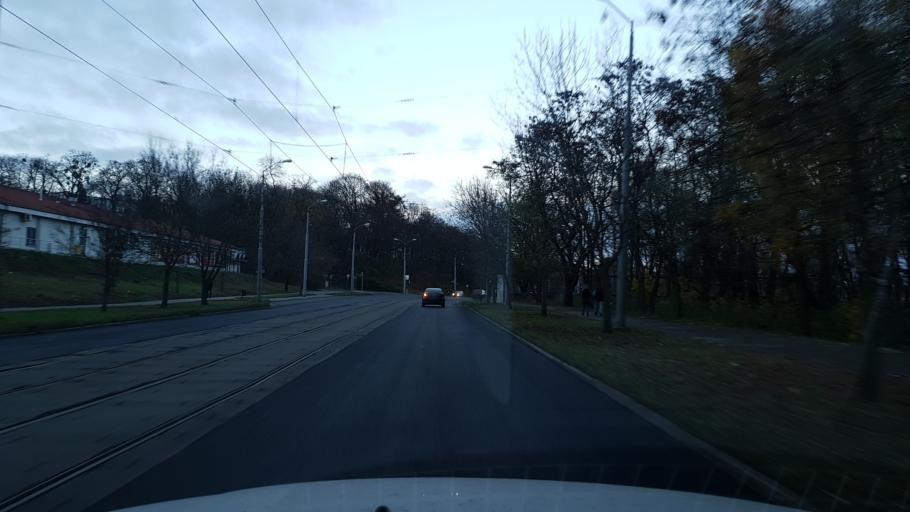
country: PL
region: West Pomeranian Voivodeship
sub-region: Szczecin
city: Szczecin
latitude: 53.4553
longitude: 14.5856
